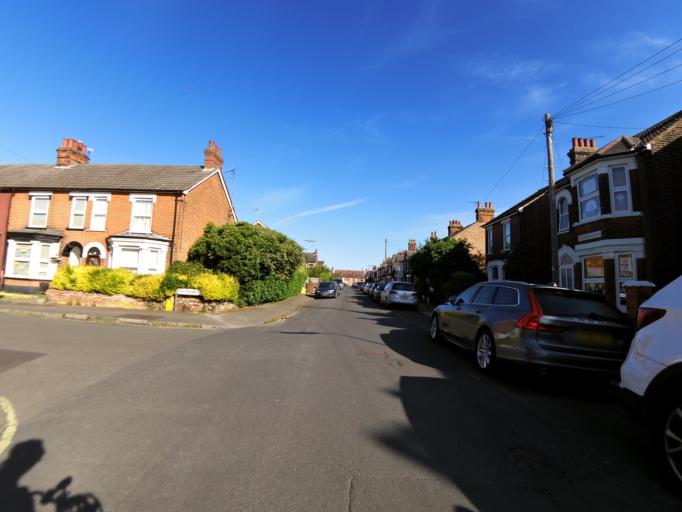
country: GB
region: England
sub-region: Suffolk
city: Ipswich
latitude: 52.0539
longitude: 1.1787
